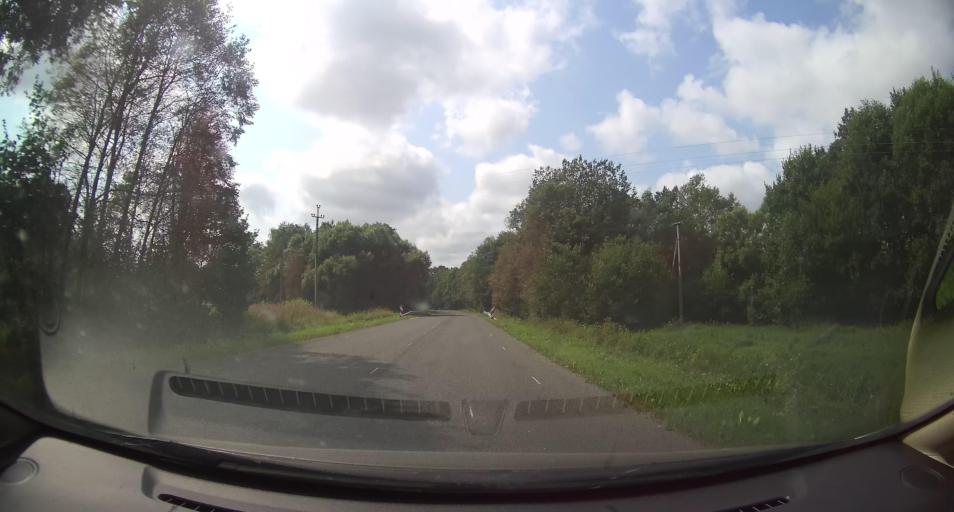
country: EE
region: Paernumaa
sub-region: Audru vald
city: Audru
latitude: 58.5005
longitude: 24.3429
